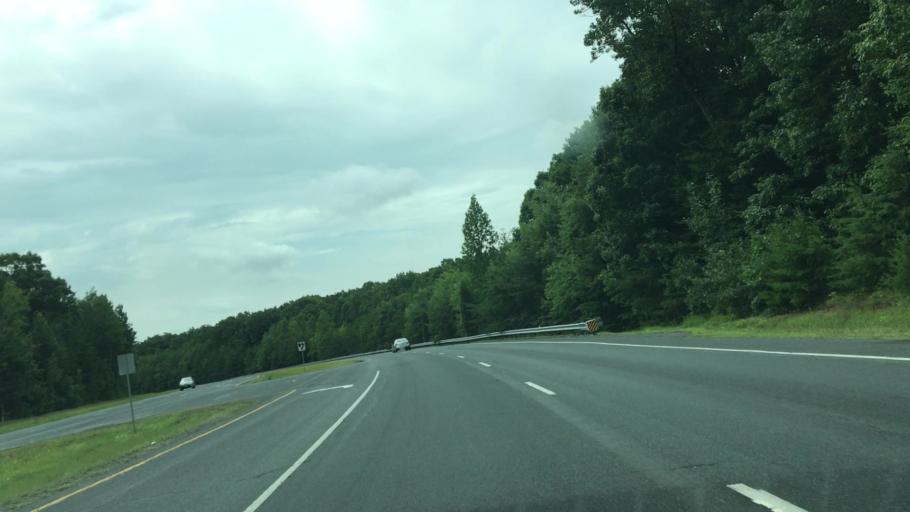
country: US
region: Virginia
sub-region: Prince William County
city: Buckhall
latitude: 38.6900
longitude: -77.3888
